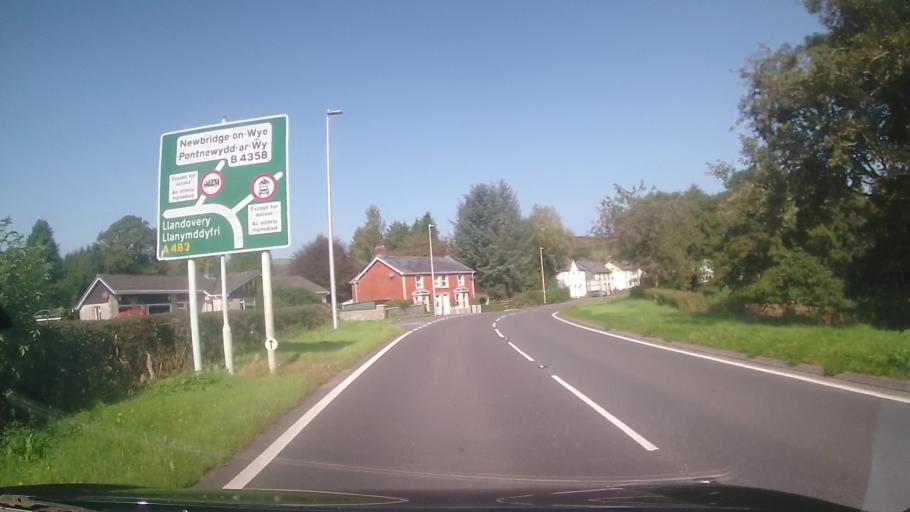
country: GB
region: Wales
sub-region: Sir Powys
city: Rhayader
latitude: 52.1472
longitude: -3.5779
